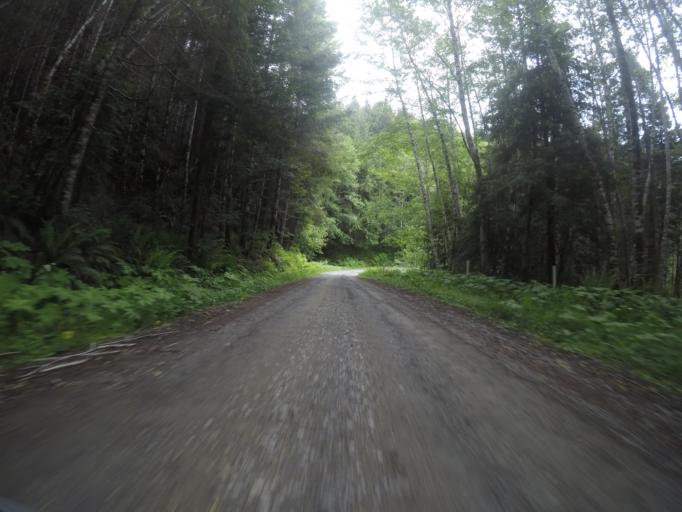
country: US
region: California
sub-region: Humboldt County
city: Westhaven-Moonstone
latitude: 41.2300
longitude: -123.9899
